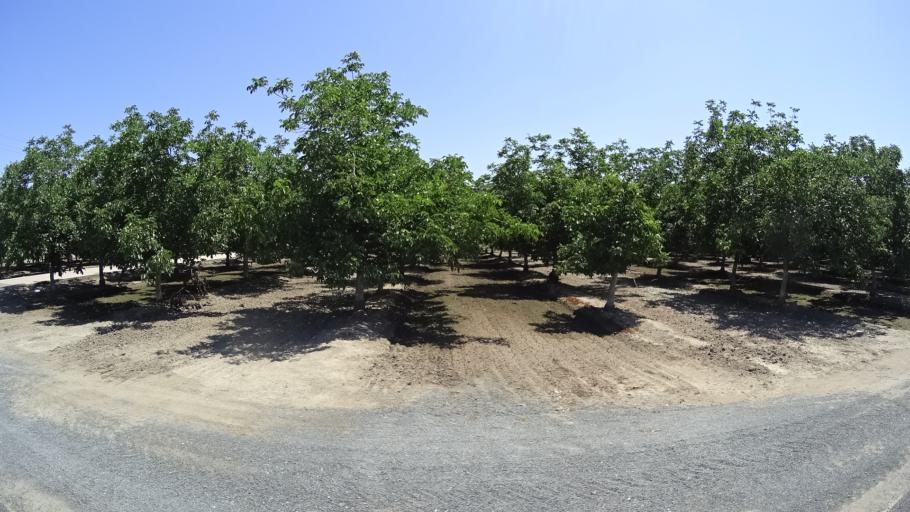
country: US
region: California
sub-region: Kings County
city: Lucerne
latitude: 36.4043
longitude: -119.6730
